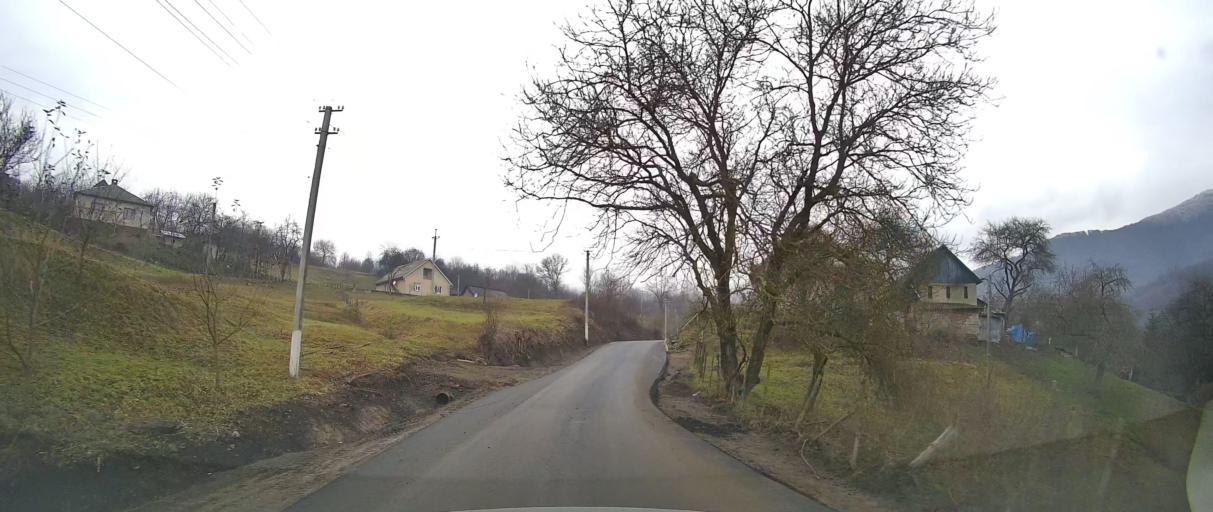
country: UA
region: Zakarpattia
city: Velykyi Bereznyi
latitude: 48.9637
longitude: 22.5487
